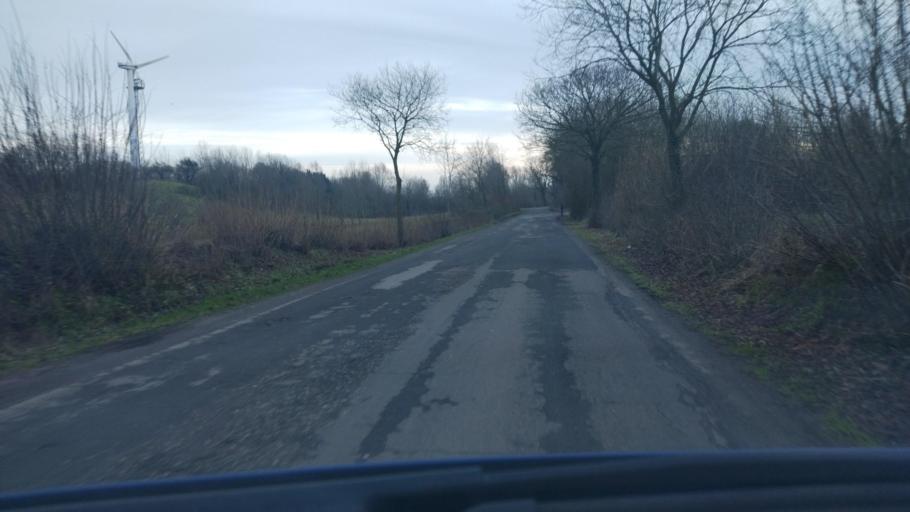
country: DE
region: Schleswig-Holstein
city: Neuberend
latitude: 54.5389
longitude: 9.5489
